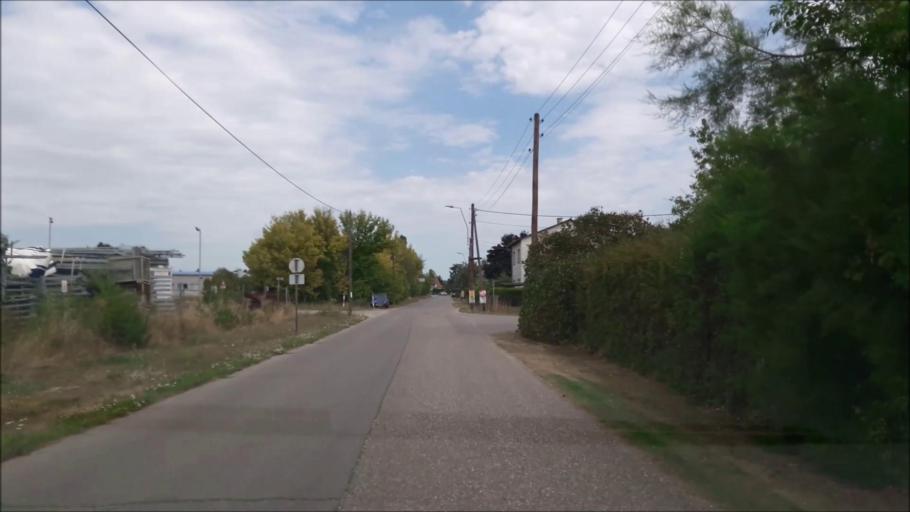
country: AT
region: Lower Austria
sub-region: Politischer Bezirk Ganserndorf
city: Parbasdorf
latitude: 48.3105
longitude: 16.6160
